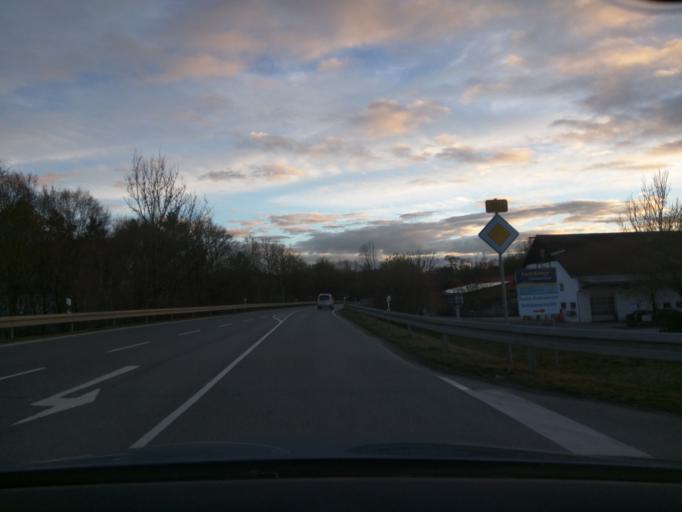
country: DE
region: Bavaria
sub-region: Upper Bavaria
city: Zolling
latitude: 48.4484
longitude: 11.7653
